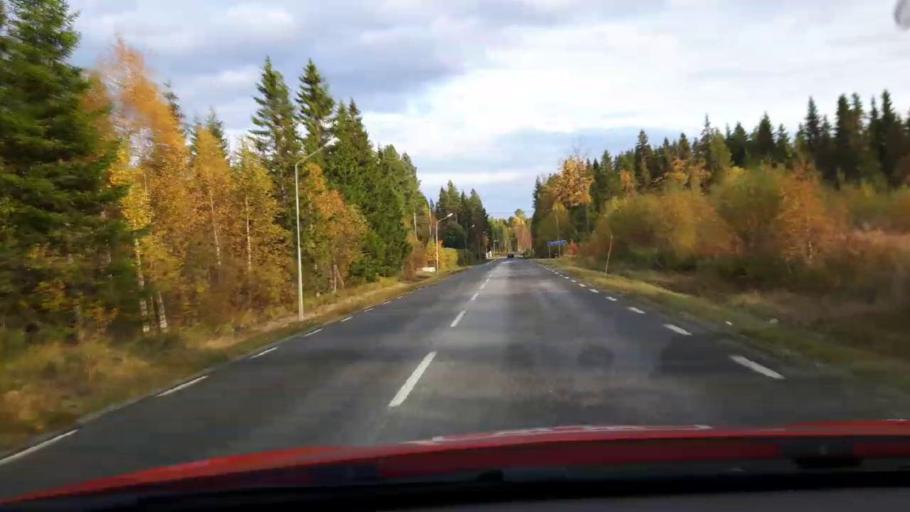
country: SE
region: Jaemtland
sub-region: Krokoms Kommun
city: Krokom
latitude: 63.3484
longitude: 14.5572
